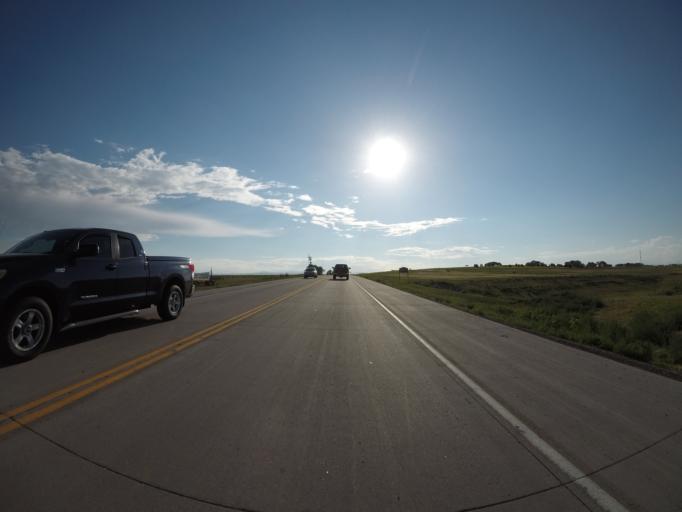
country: US
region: Colorado
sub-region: Weld County
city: Severance
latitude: 40.5815
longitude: -104.8988
